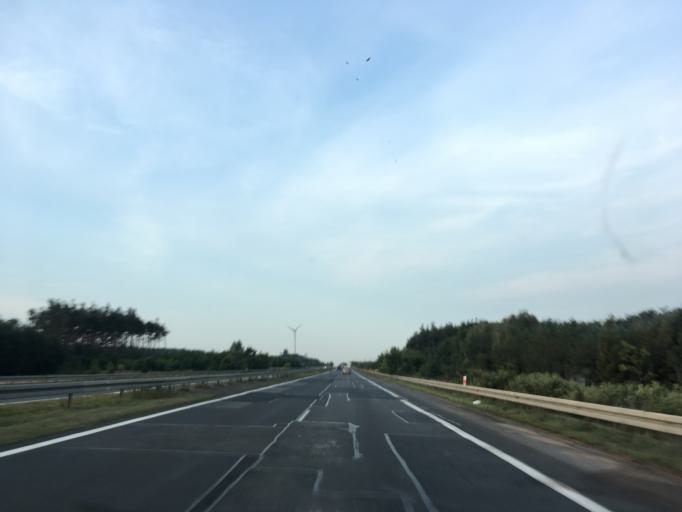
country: PL
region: Lodz Voivodeship
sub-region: Powiat radomszczanski
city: Gomunice
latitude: 51.1550
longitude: 19.4443
